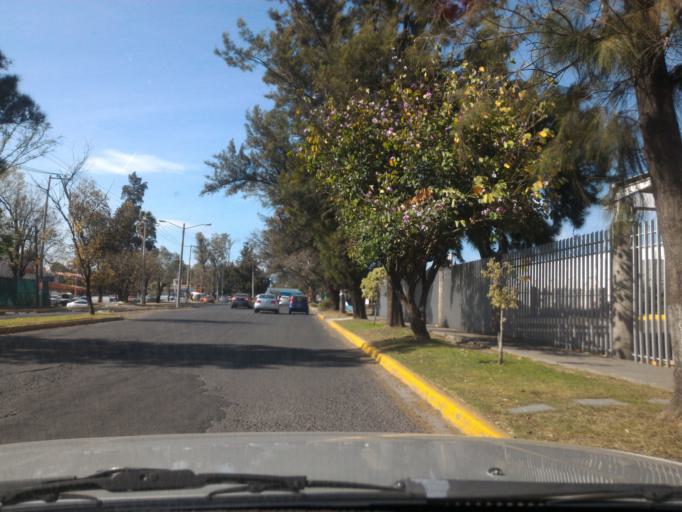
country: MX
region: Jalisco
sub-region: Tlajomulco de Zuniga
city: La Tijera
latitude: 20.6172
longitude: -103.4220
